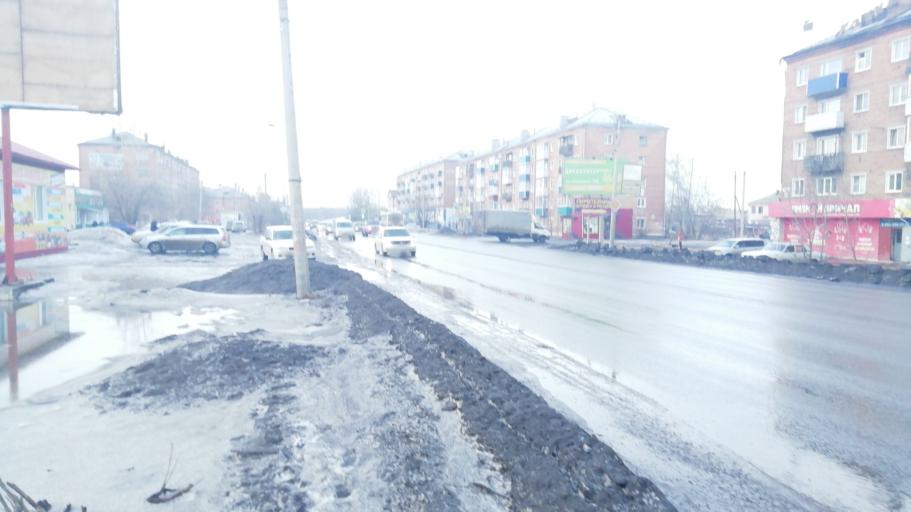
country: RU
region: Krasnoyarskiy
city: Kansk
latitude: 56.1946
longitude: 95.7205
